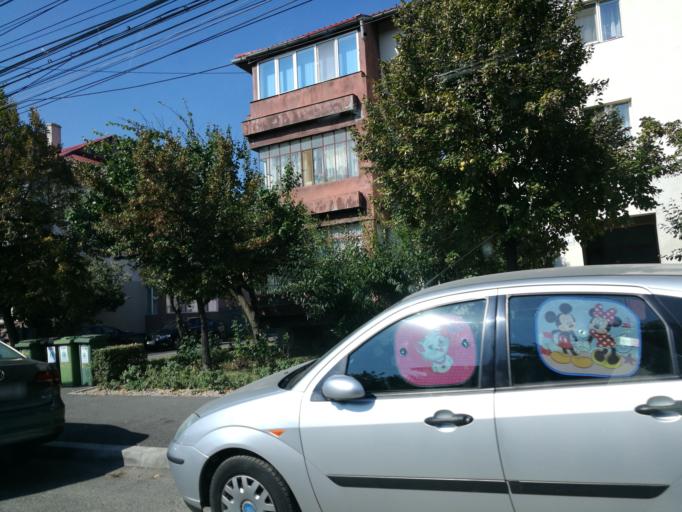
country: RO
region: Ilfov
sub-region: Comuna Otopeni
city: Otopeni
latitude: 44.5511
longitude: 26.0756
